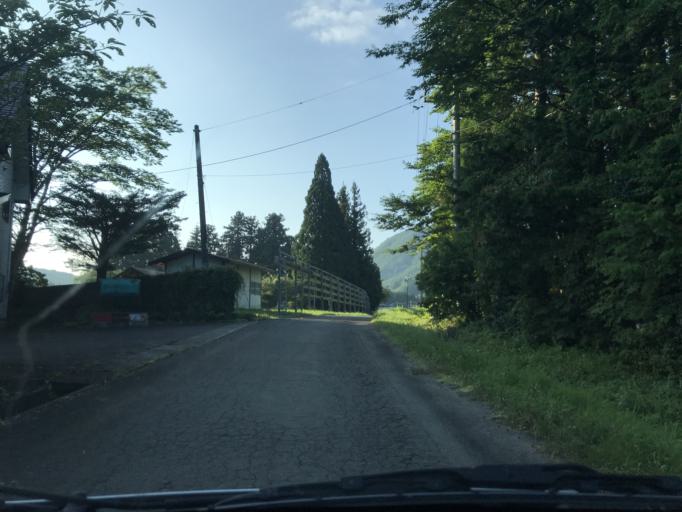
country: JP
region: Iwate
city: Ichinoseki
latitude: 38.9770
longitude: 140.9213
